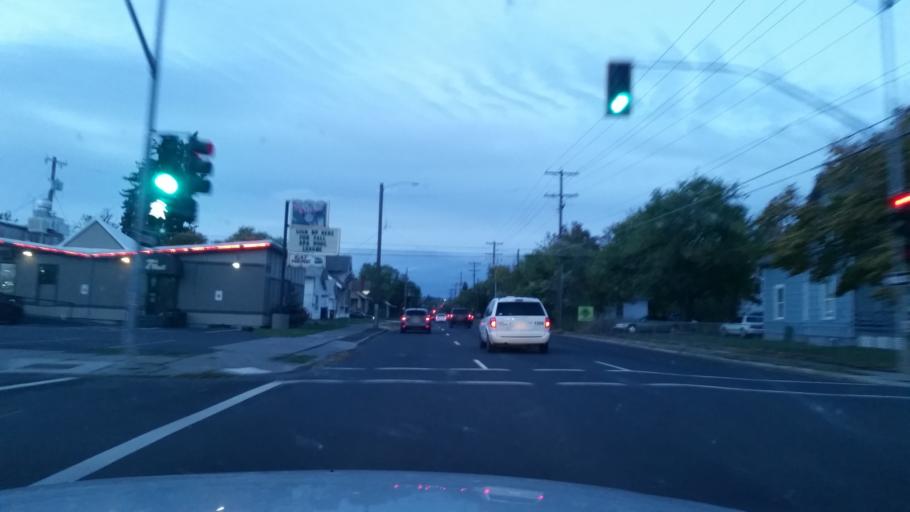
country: US
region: Washington
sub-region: Spokane County
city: Spokane
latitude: 47.6749
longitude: -117.4356
